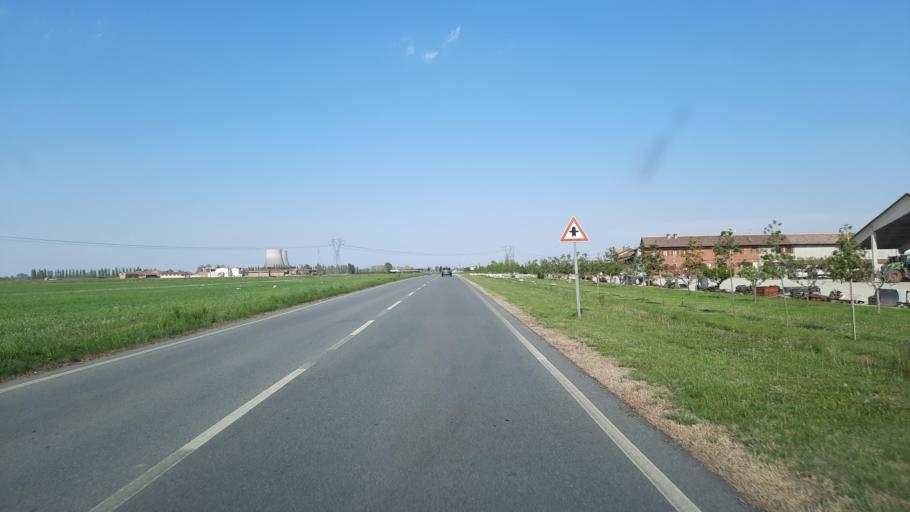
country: IT
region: Piedmont
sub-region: Provincia di Vercelli
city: Fontanetto Po
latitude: 45.2353
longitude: 8.1680
